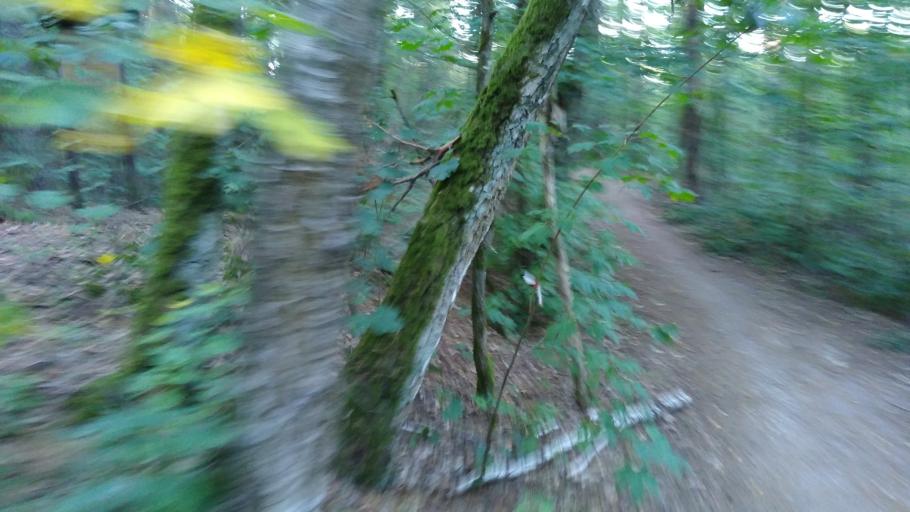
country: DE
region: Bavaria
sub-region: Regierungsbezirk Mittelfranken
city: Zirndorf
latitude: 49.4680
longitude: 10.9325
